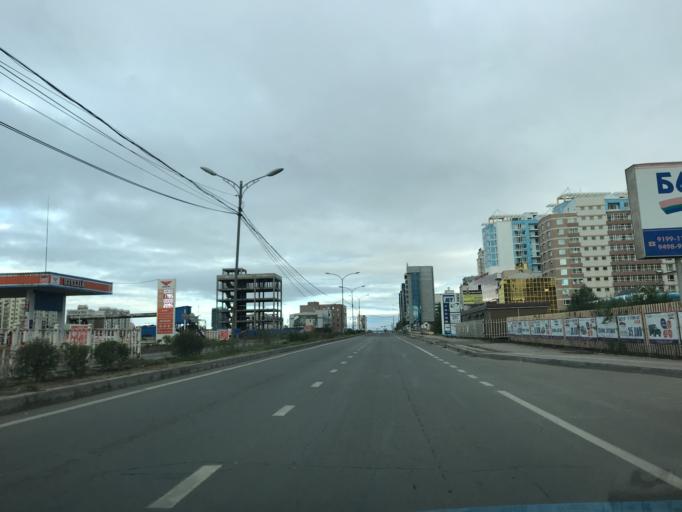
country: MN
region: Ulaanbaatar
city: Ulaanbaatar
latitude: 47.9082
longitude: 106.9357
